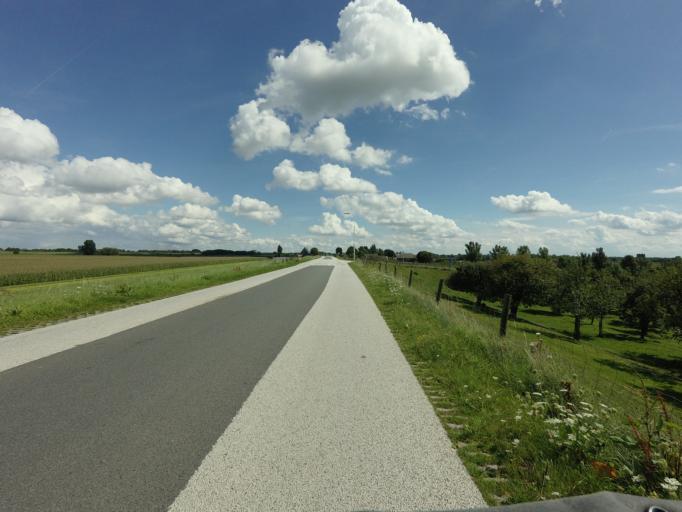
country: NL
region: Utrecht
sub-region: Gemeente Lopik
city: Lopik
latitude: 51.9741
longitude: 5.0033
